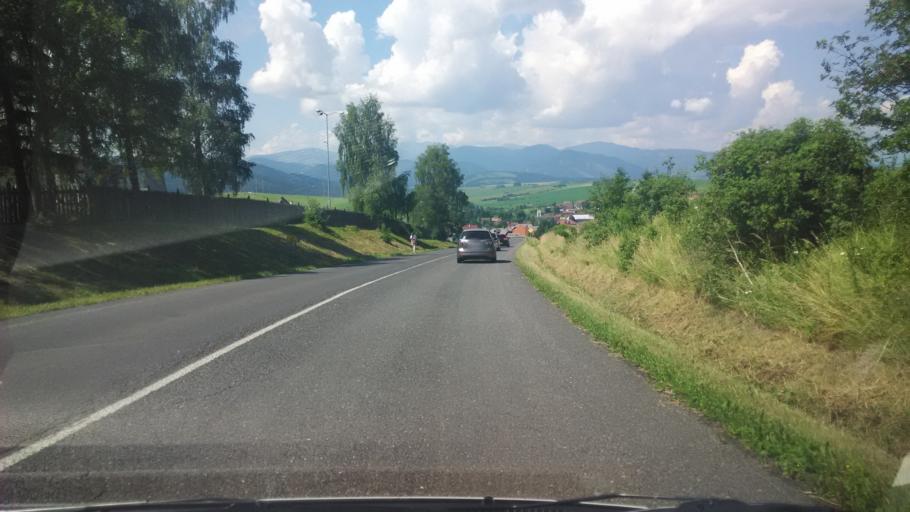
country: SK
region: Zilinsky
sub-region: Okres Liptovsky Mikulas
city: Hybe
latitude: 49.0624
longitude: 19.9012
